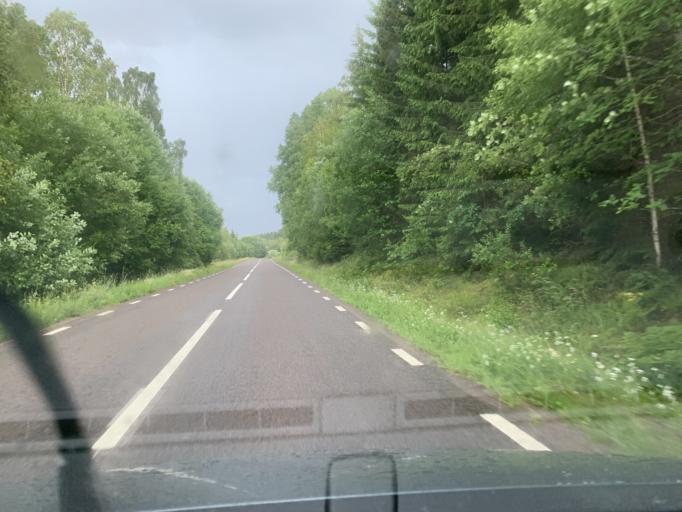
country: SE
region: Kalmar
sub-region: Vasterviks Kommun
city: Overum
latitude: 58.0195
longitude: 16.1456
